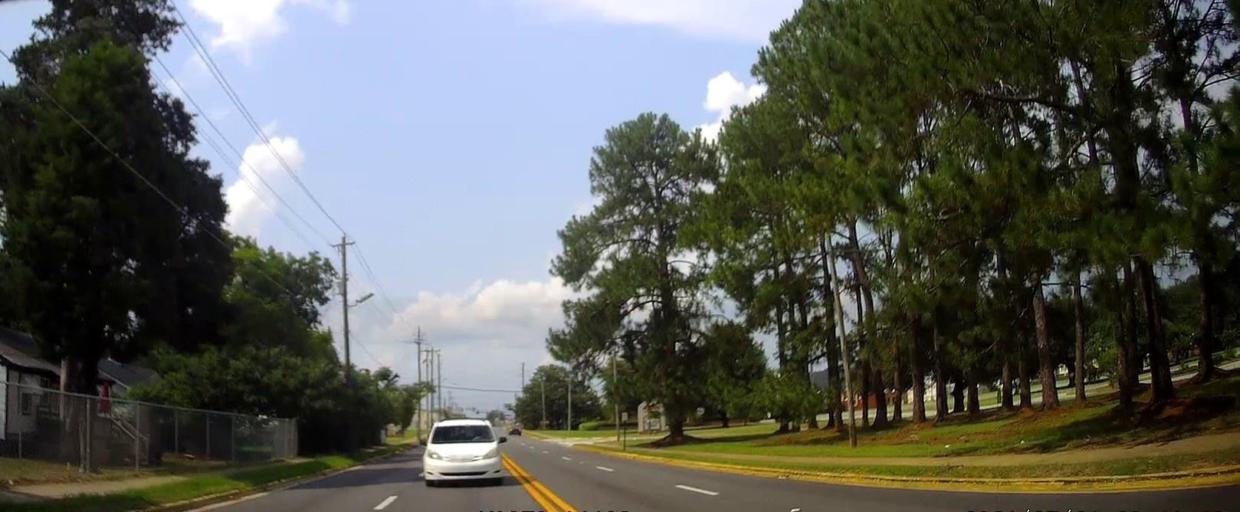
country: US
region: Georgia
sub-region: Houston County
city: Warner Robins
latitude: 32.6153
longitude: -83.6131
